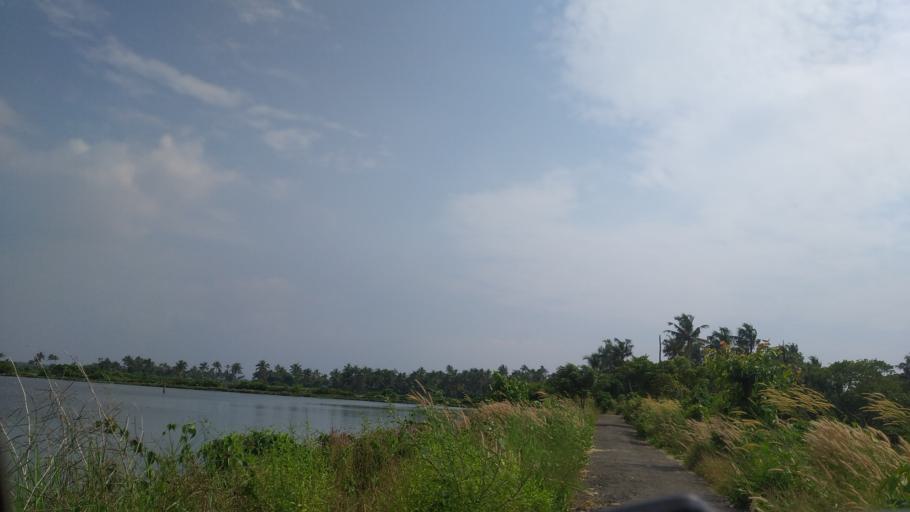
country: IN
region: Kerala
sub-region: Ernakulam
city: Elur
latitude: 10.0857
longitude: 76.2185
